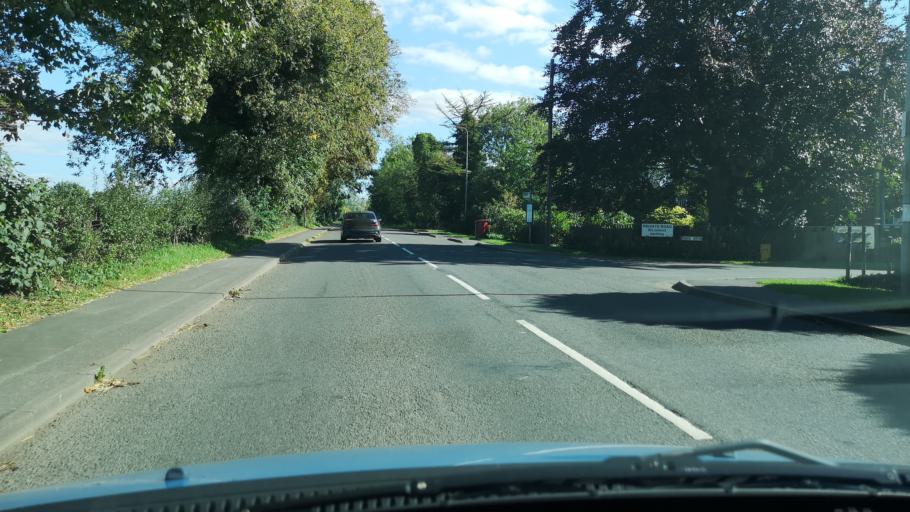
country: GB
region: England
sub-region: North Lincolnshire
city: Crowle
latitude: 53.5989
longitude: -0.8259
